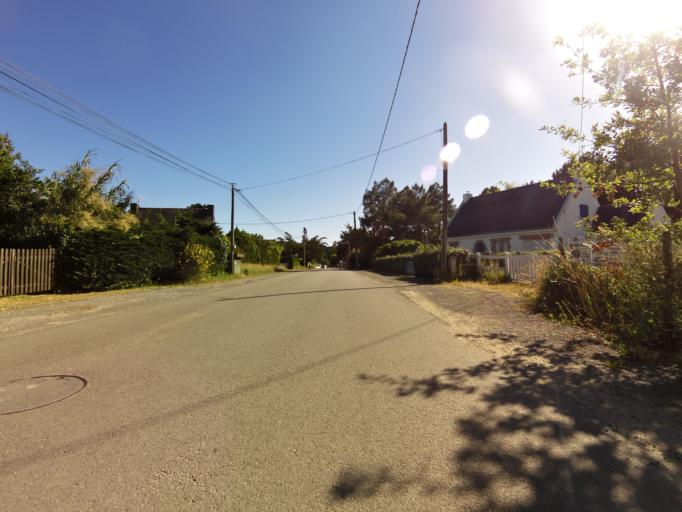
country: FR
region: Brittany
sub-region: Departement du Morbihan
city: Penestin
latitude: 47.4700
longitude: -2.4857
